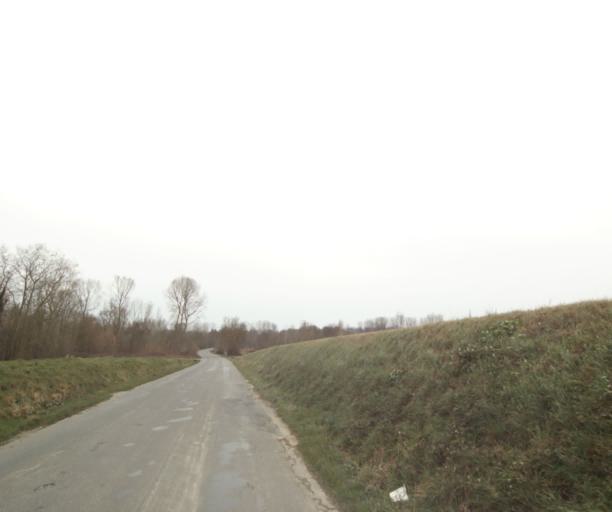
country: FR
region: Poitou-Charentes
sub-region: Departement des Deux-Sevres
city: Bessines
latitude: 46.3087
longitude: -0.5167
